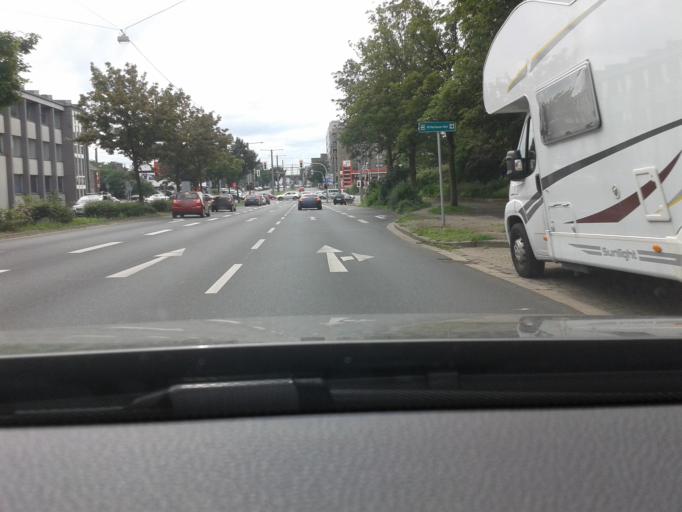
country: DE
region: North Rhine-Westphalia
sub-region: Regierungsbezirk Dusseldorf
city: Oberhausen
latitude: 51.4714
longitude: 6.8638
